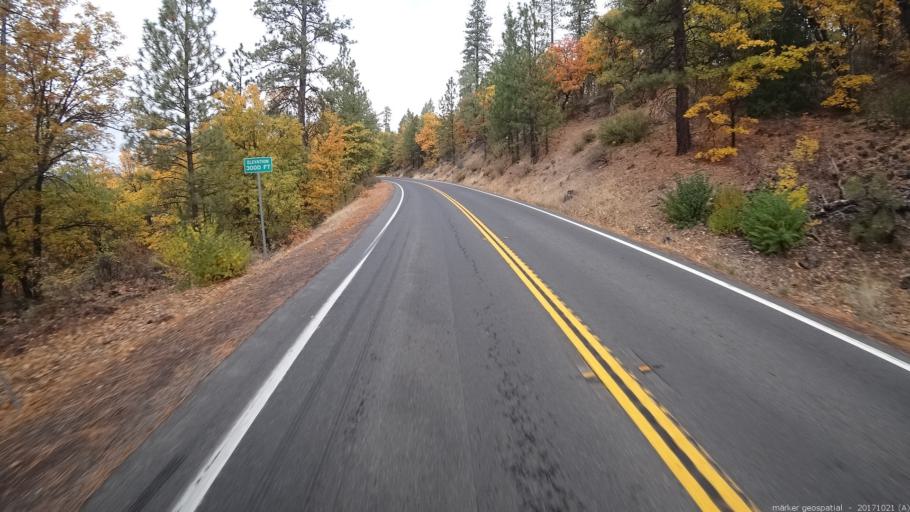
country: US
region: California
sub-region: Shasta County
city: Burney
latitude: 41.0274
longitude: -121.6256
